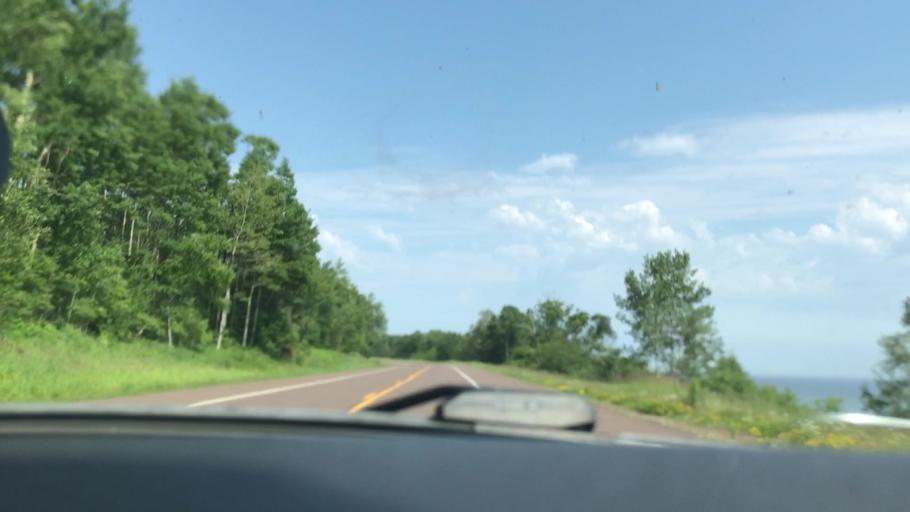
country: US
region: Minnesota
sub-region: Cook County
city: Grand Marais
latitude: 47.7765
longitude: -90.2074
